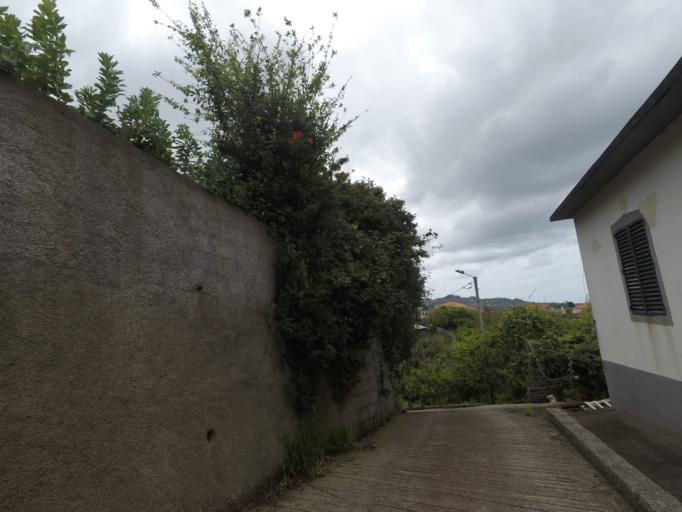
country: PT
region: Madeira
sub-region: Santana
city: Santana
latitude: 32.8070
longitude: -16.8787
